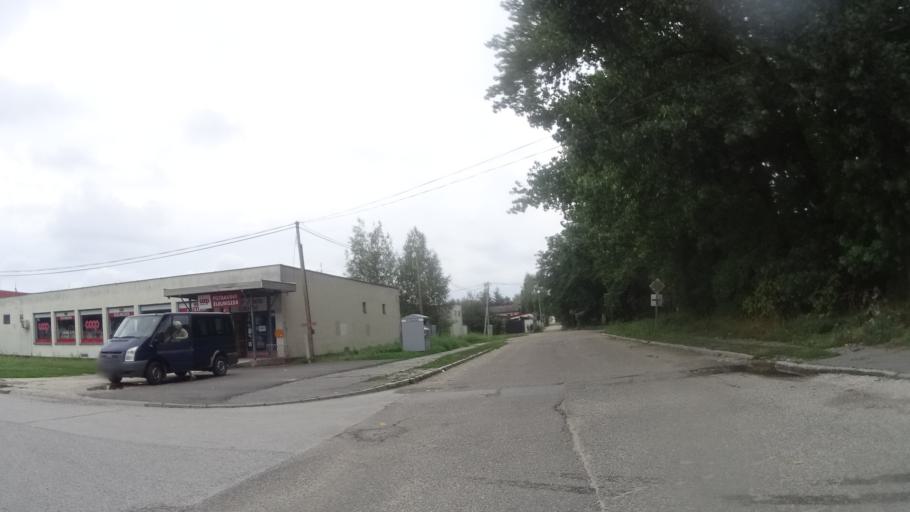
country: HU
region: Komarom-Esztergom
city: Komarom
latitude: 47.7629
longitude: 18.0554
